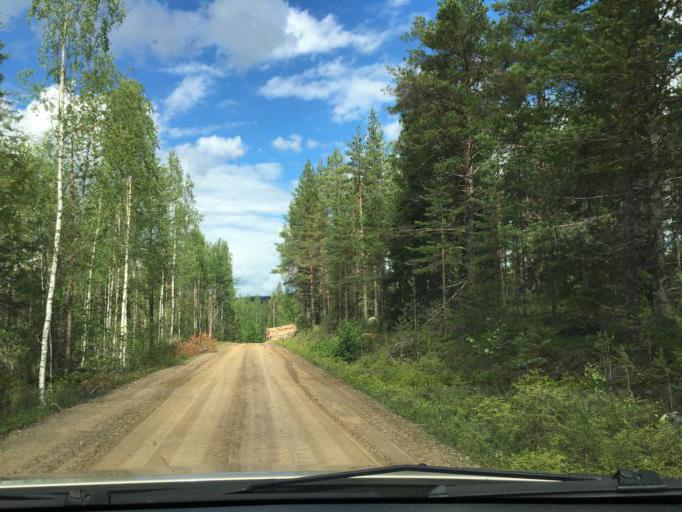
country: SE
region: Norrbotten
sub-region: Overkalix Kommun
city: OEverkalix
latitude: 66.1496
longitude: 22.7971
